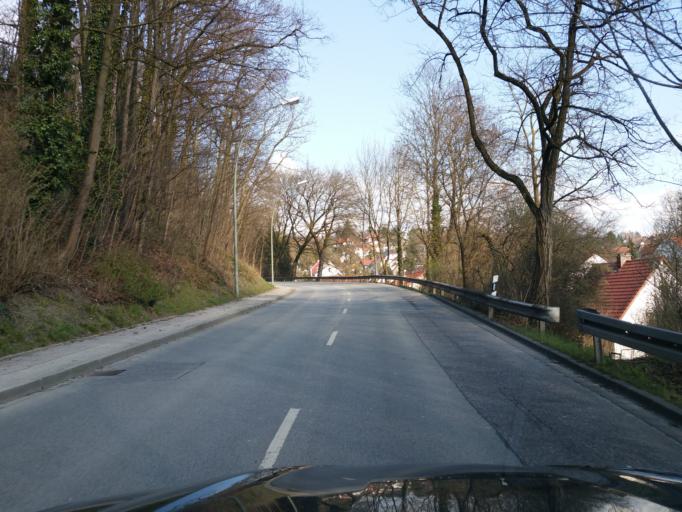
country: DE
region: Bavaria
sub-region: Lower Bavaria
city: Landshut
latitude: 48.5259
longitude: 12.1490
